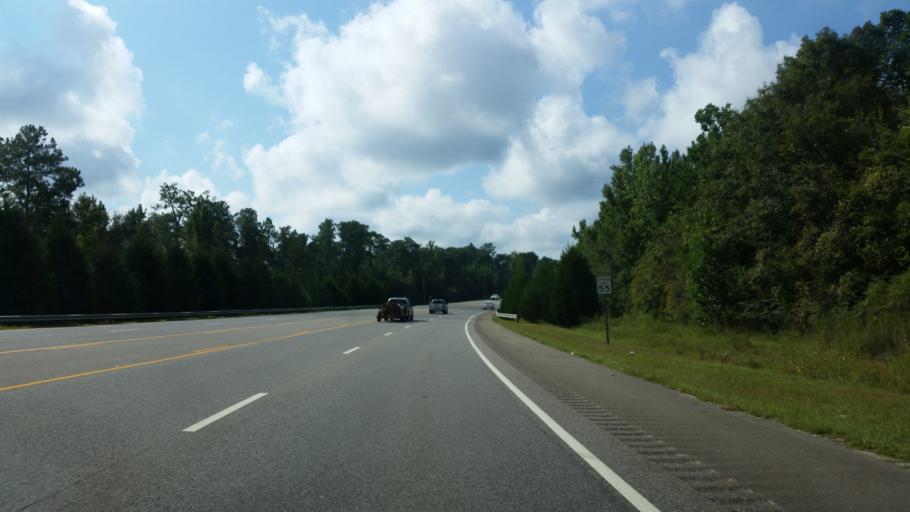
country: US
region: Alabama
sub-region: Baldwin County
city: Bay Minette
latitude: 30.9528
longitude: -87.7614
